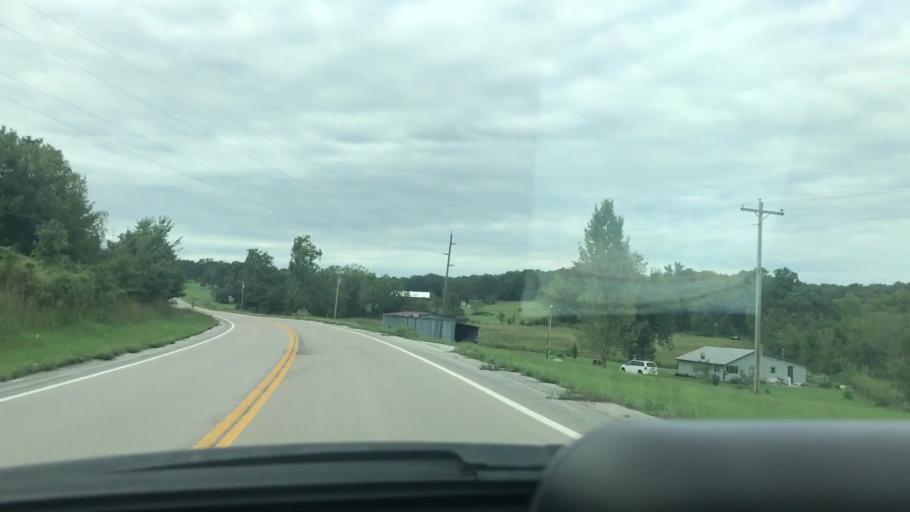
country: US
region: Missouri
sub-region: Benton County
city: Warsaw
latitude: 38.1329
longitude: -93.2805
